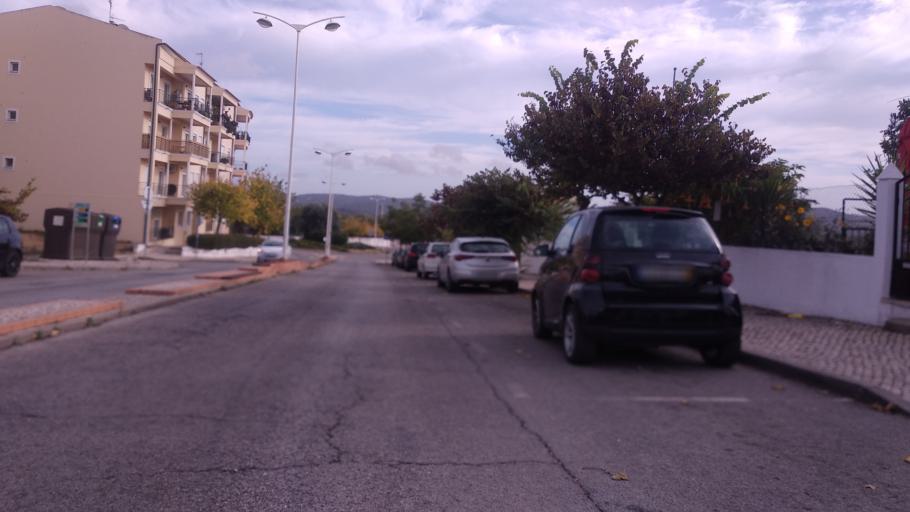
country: PT
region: Faro
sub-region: Sao Bras de Alportel
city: Sao Bras de Alportel
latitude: 37.1516
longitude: -7.8943
